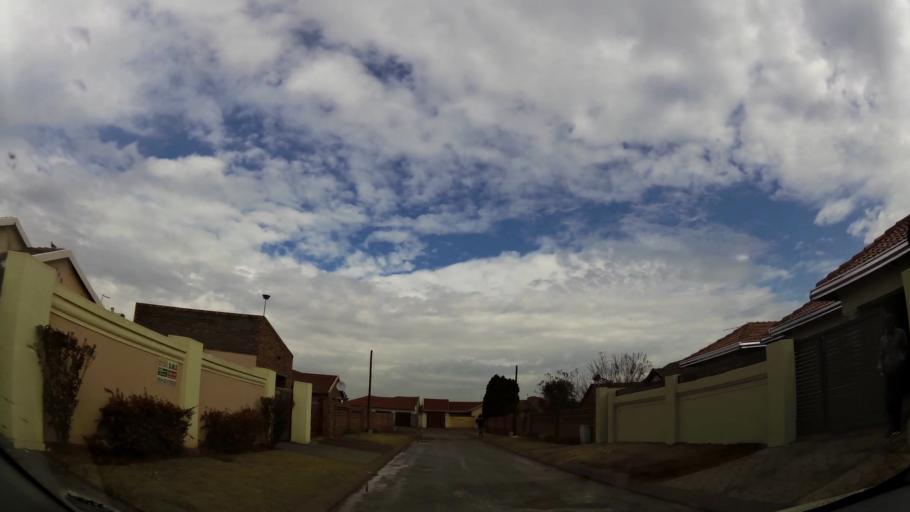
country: ZA
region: Gauteng
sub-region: Ekurhuleni Metropolitan Municipality
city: Germiston
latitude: -26.3246
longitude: 28.1933
